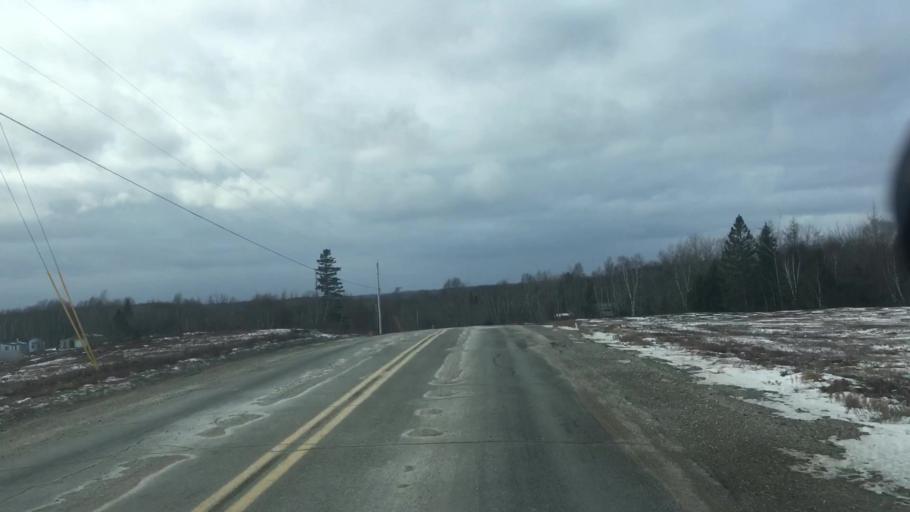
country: US
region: Maine
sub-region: Washington County
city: Machias
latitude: 44.6556
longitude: -67.5204
